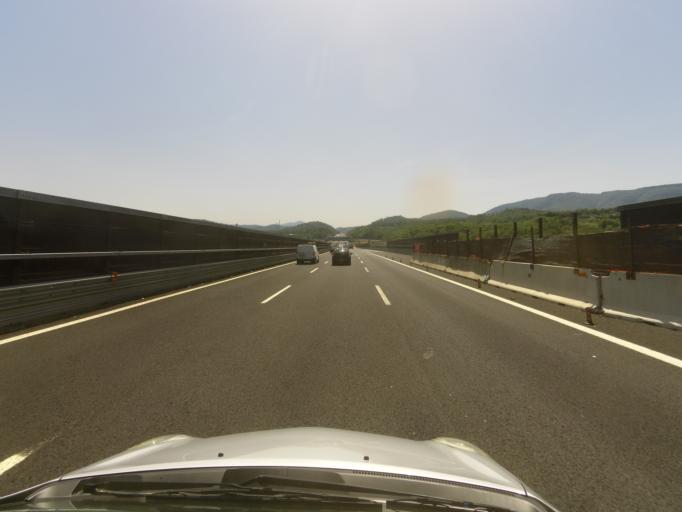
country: IT
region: Tuscany
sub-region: Province of Florence
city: Cavallina
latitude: 43.9894
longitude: 11.2109
